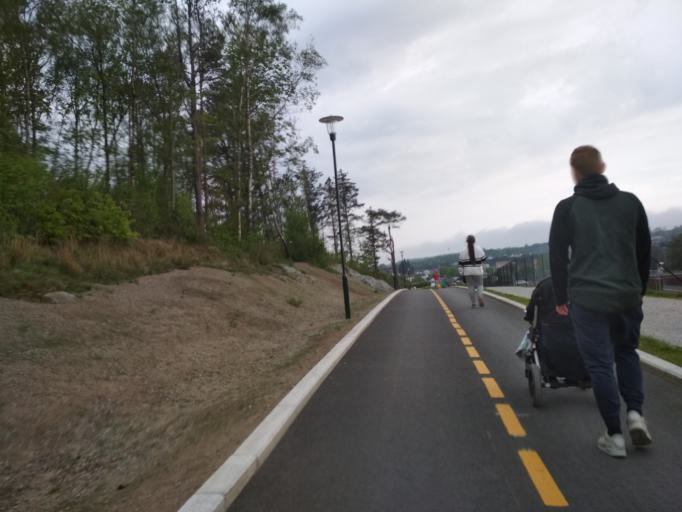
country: NO
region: Rogaland
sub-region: Stavanger
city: Stavanger
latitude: 58.9546
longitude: 5.7226
